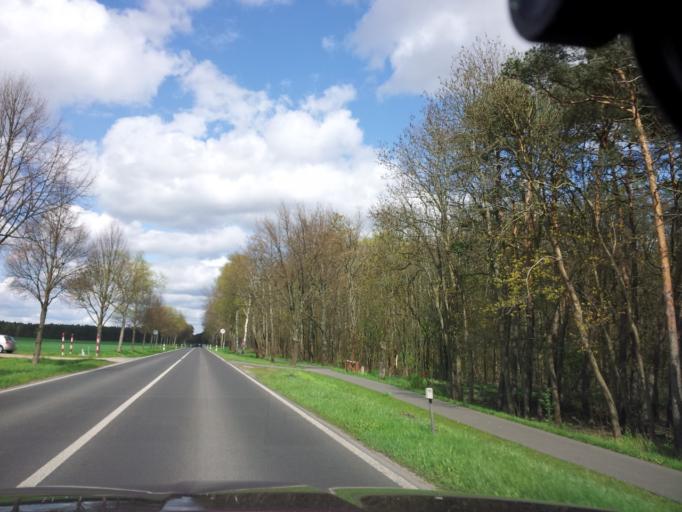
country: DE
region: Brandenburg
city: Bernau bei Berlin
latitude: 52.6980
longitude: 13.6078
